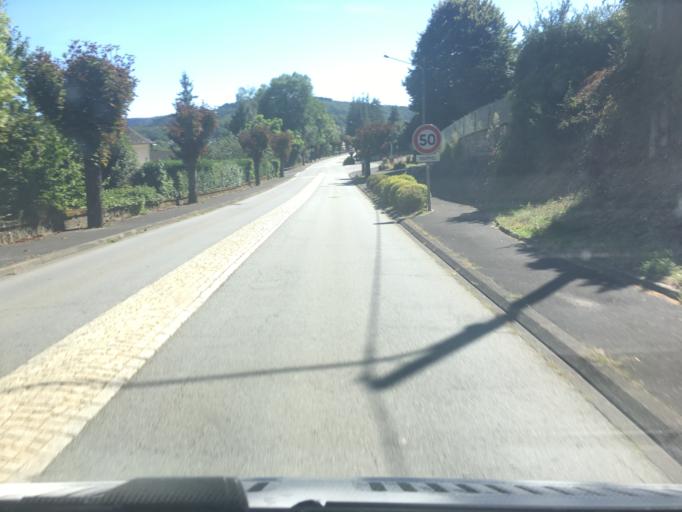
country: FR
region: Limousin
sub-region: Departement de la Correze
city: Bort-les-Orgues
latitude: 45.4013
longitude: 2.4936
